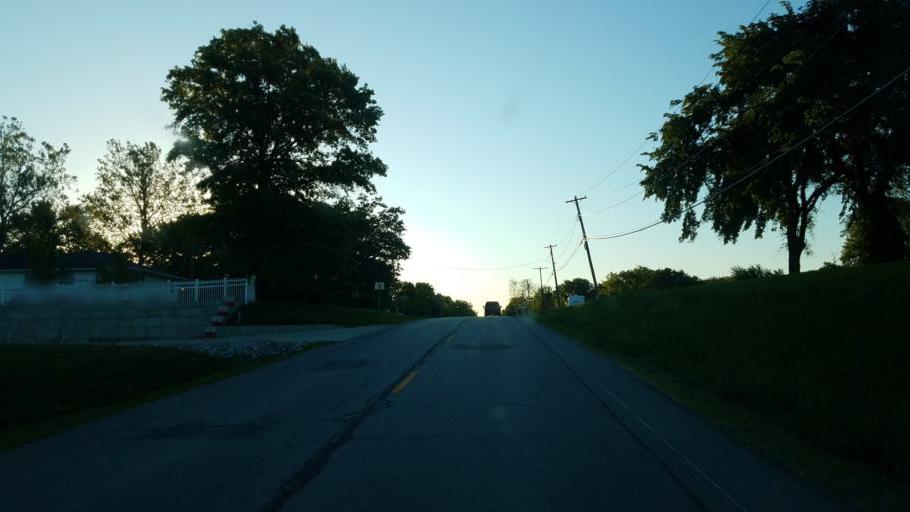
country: US
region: Missouri
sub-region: Schuyler County
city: Lancaster
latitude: 40.5223
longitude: -92.5376
